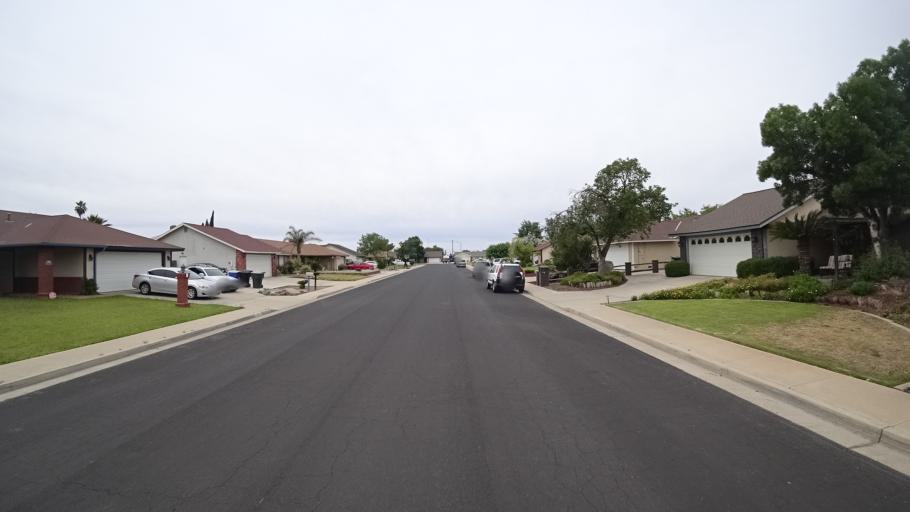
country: US
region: California
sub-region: Kings County
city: Hanford
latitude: 36.3475
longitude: -119.6303
